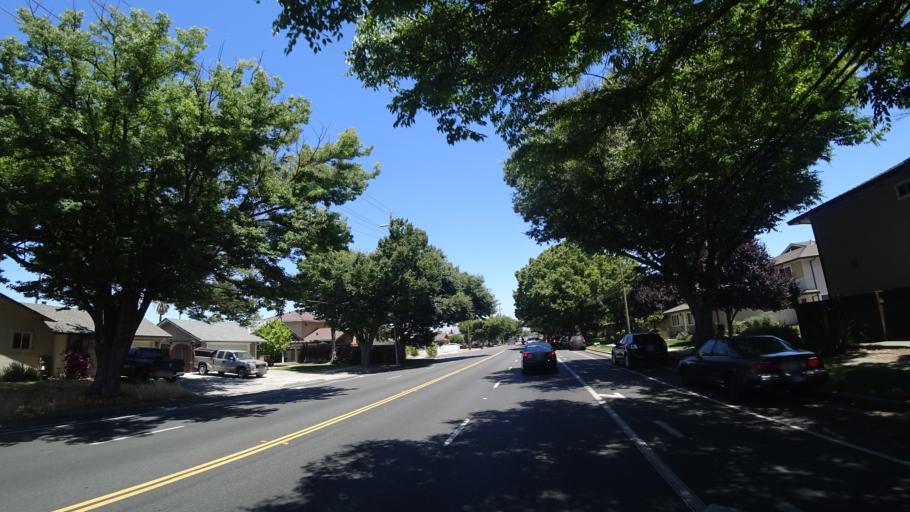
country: US
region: California
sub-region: Santa Clara County
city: Cambrian Park
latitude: 37.2596
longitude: -121.8892
